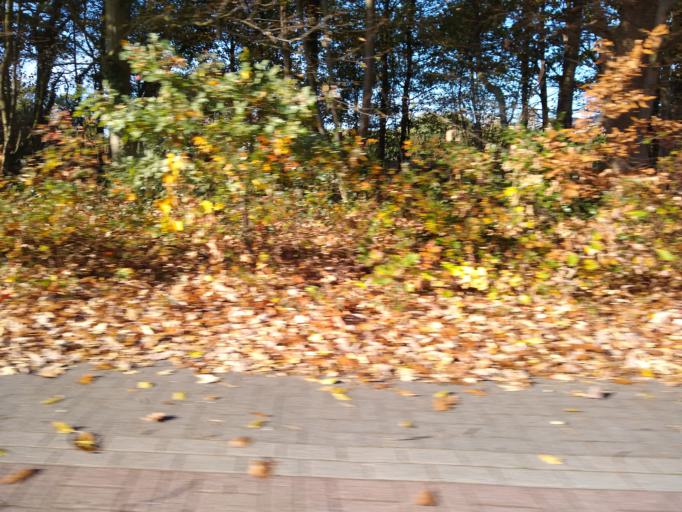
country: DE
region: Lower Saxony
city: Oldenburg
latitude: 53.1872
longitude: 8.2021
